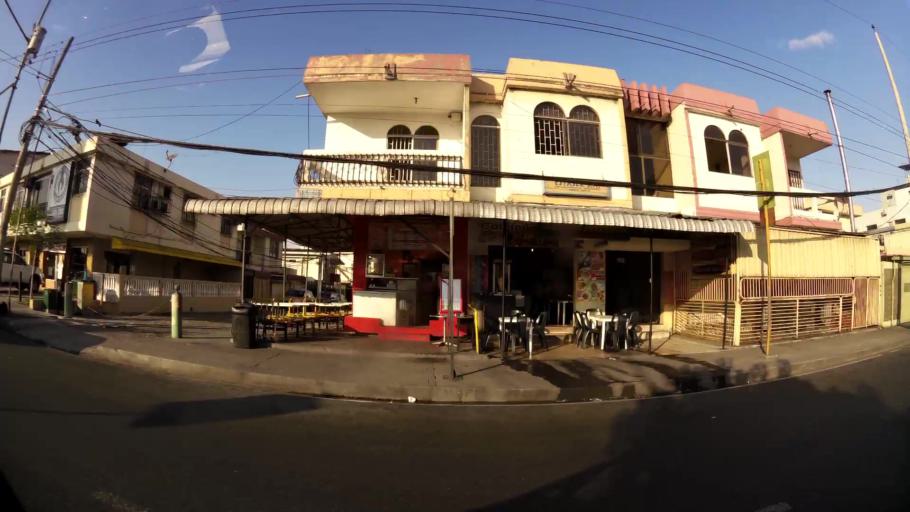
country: EC
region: Guayas
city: Guayaquil
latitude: -2.1721
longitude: -79.8986
